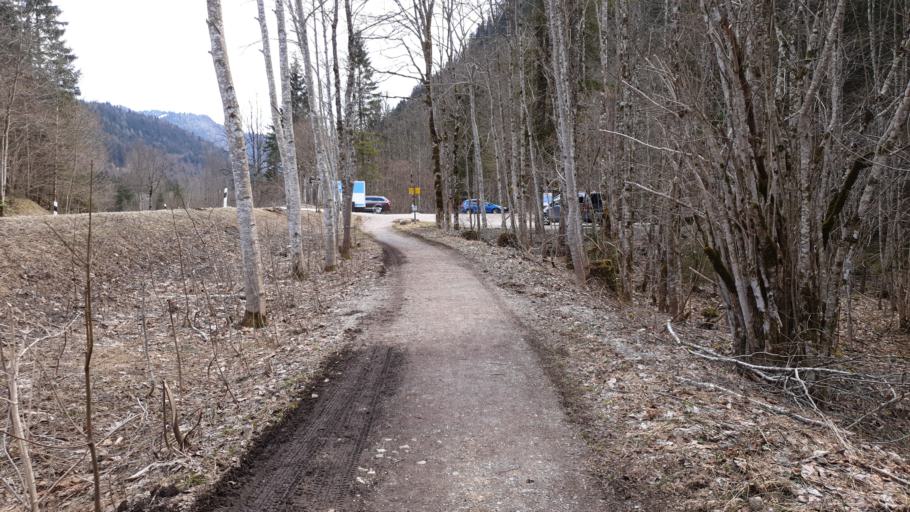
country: DE
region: Bavaria
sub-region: Upper Bavaria
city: Bayrischzell
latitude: 47.6451
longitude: 12.0086
